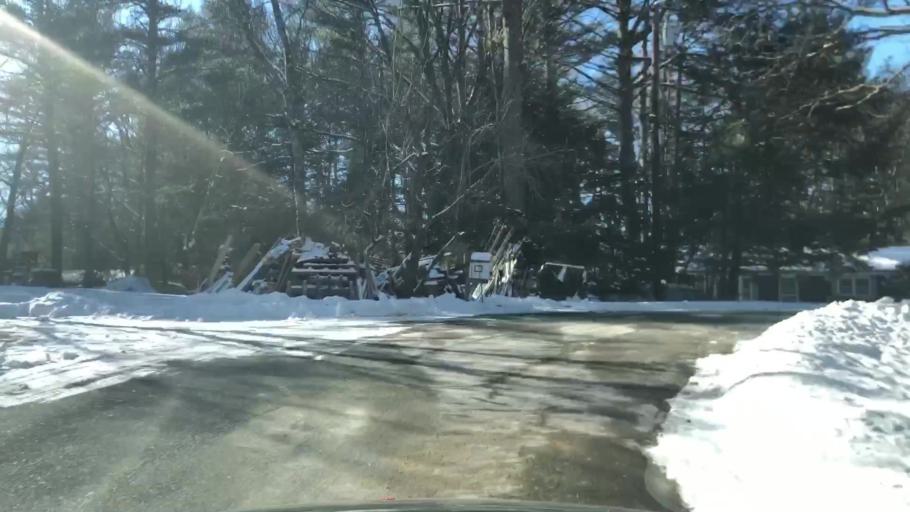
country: US
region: New Hampshire
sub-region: Hillsborough County
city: Bedford
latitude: 42.9399
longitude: -71.5358
